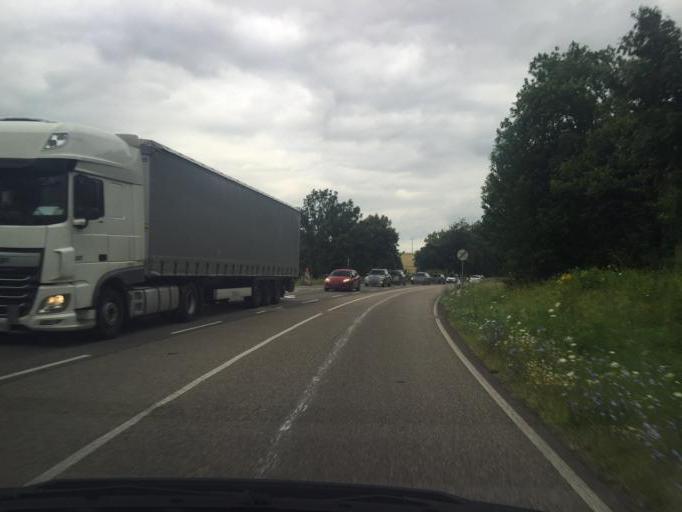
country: DE
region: Baden-Wuerttemberg
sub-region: Karlsruhe Region
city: Gondelsheim
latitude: 49.0389
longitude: 8.6715
